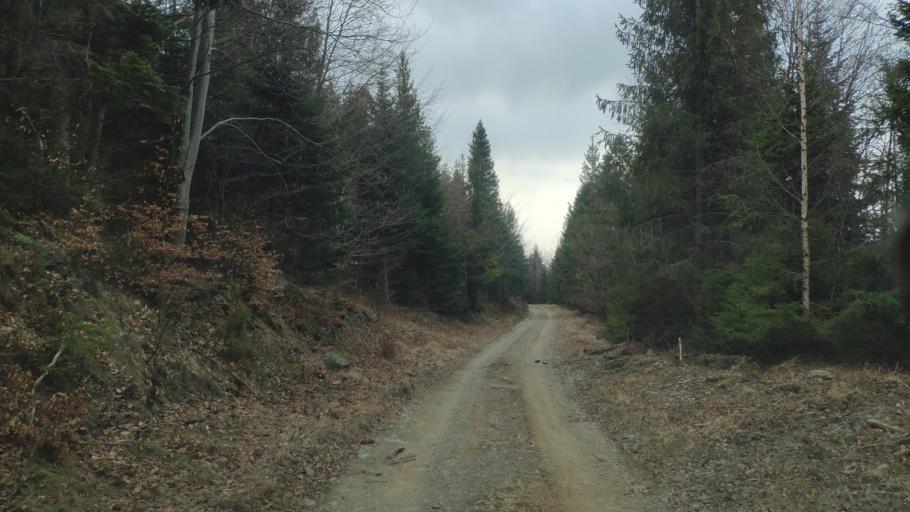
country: SK
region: Kosicky
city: Gelnica
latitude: 48.7582
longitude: 21.0401
